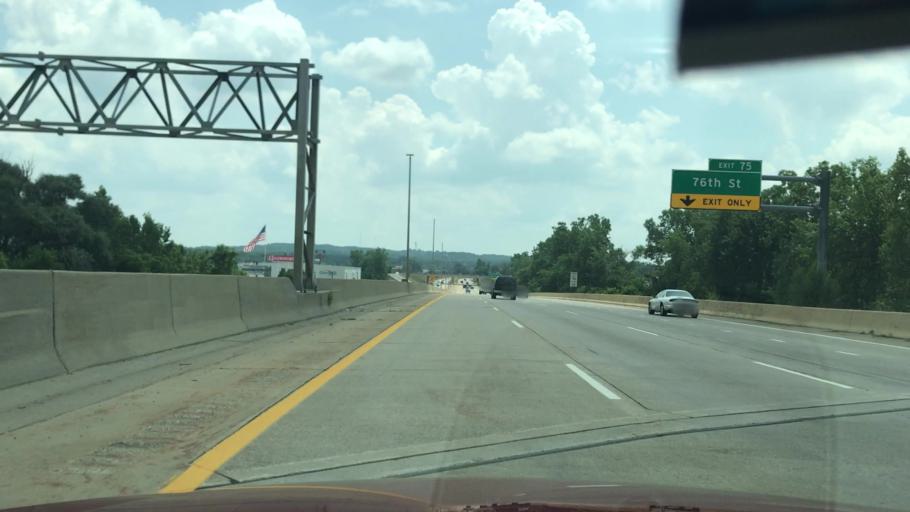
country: US
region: Michigan
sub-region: Kent County
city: Cutlerville
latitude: 42.8316
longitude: -85.6749
